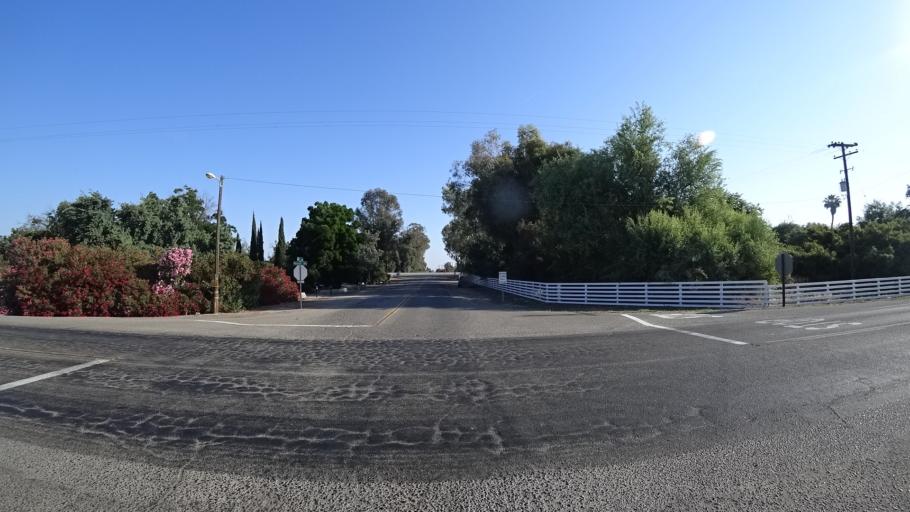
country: US
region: California
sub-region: Kings County
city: Lemoore
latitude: 36.2988
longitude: -119.7447
